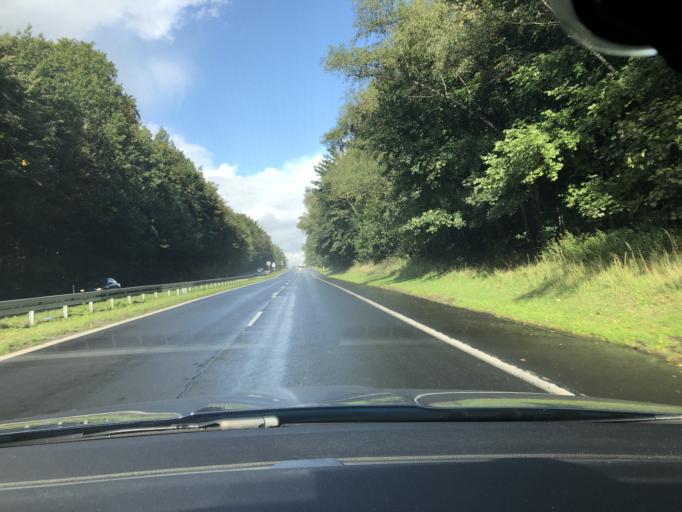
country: PL
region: Silesian Voivodeship
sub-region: Katowice
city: Murcki
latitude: 50.1878
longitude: 19.0385
